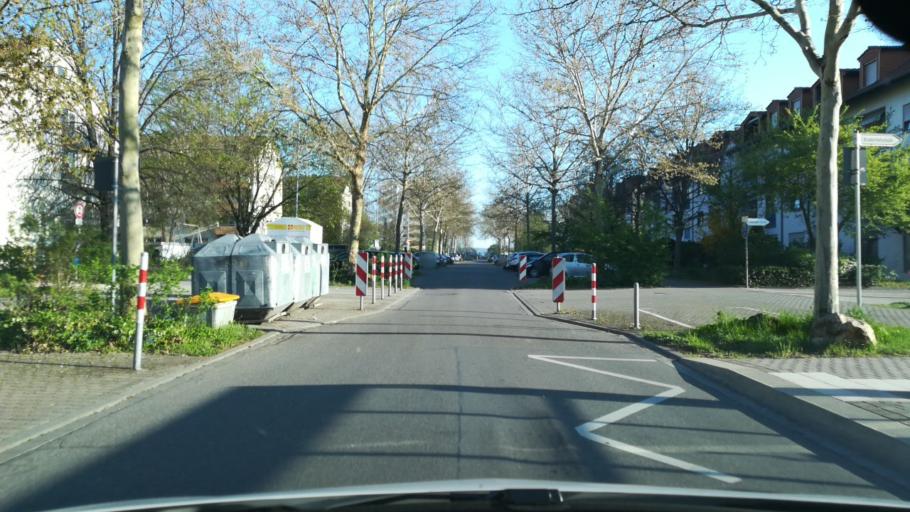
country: DE
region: Baden-Wuerttemberg
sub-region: Freiburg Region
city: Singen
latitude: 47.7765
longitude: 8.8532
